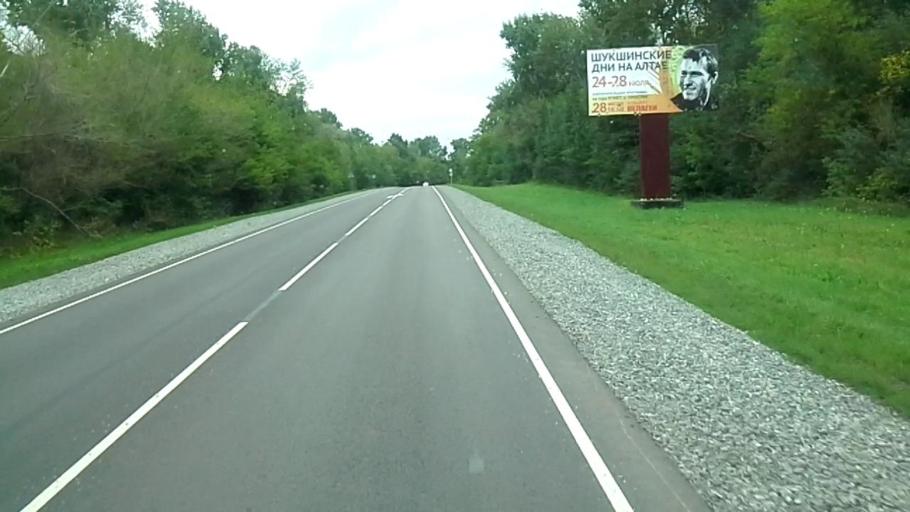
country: RU
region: Altai Krai
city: Srostki
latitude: 52.4294
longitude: 85.6721
